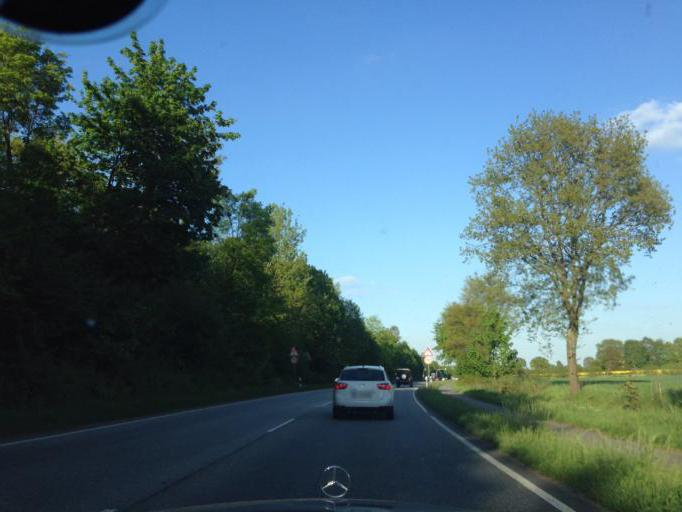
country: DE
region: Schleswig-Holstein
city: Stapelfeld
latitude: 53.6150
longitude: 10.2168
